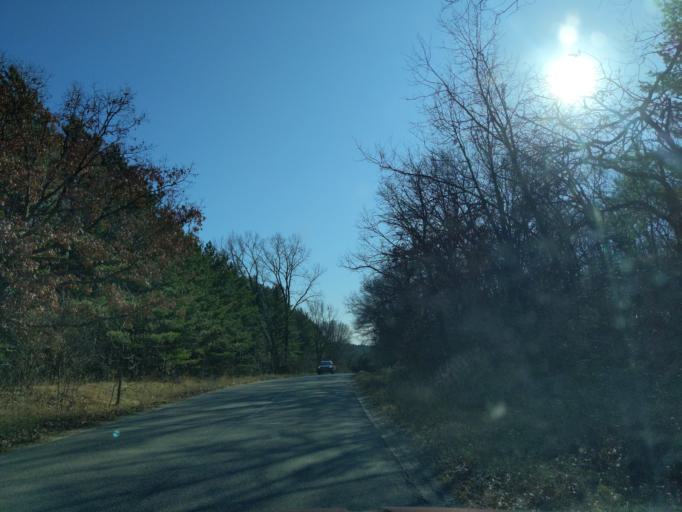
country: US
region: Wisconsin
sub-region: Waushara County
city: Wautoma
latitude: 44.1148
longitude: -89.2810
